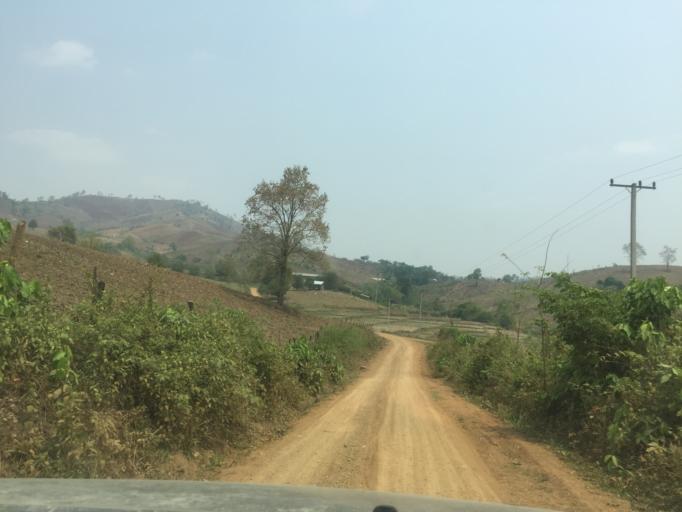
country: LA
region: Xiagnabouli
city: Muang Kenthao
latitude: 17.8098
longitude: 101.2705
